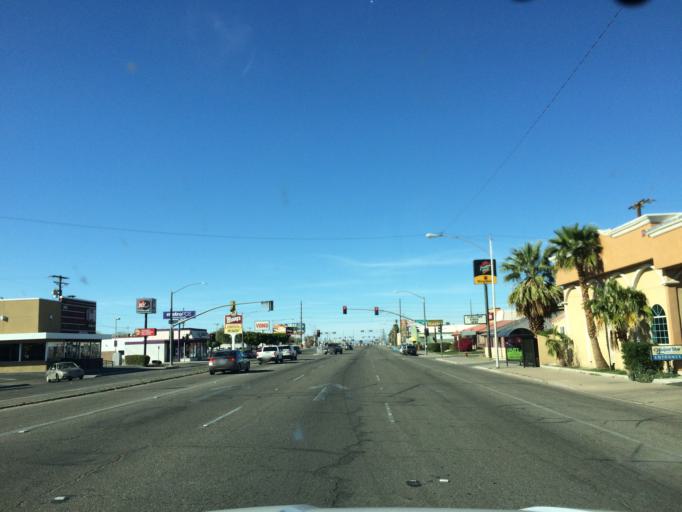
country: US
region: California
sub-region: Imperial County
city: El Centro
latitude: 32.7976
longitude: -115.5699
